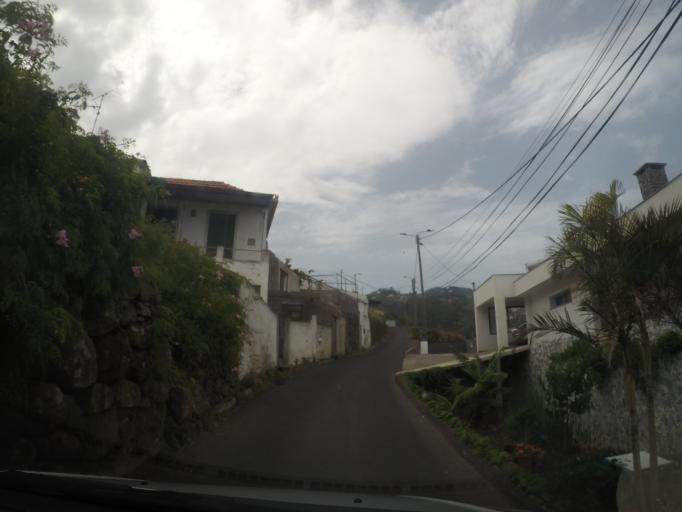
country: PT
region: Madeira
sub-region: Santa Cruz
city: Santa Cruz
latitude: 32.6859
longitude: -16.8059
